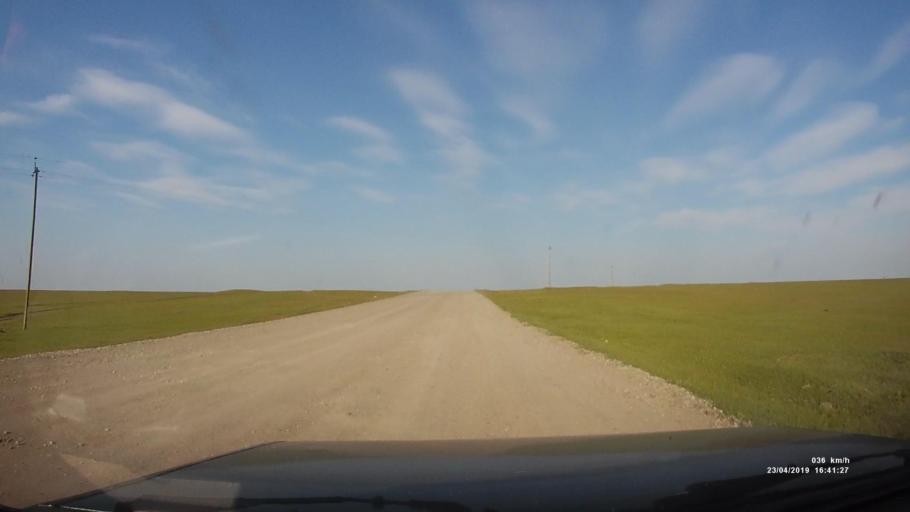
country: RU
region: Kalmykiya
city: Priyutnoye
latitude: 46.3460
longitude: 43.1868
